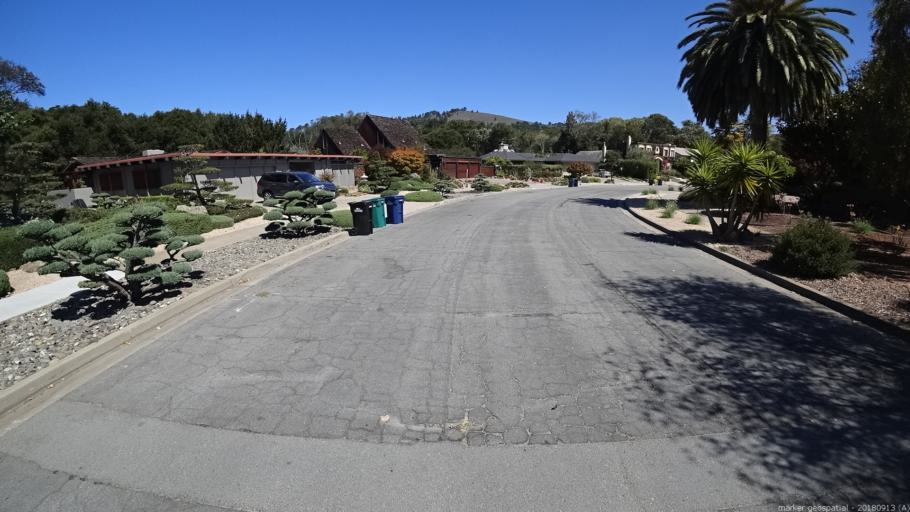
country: US
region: California
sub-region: Monterey County
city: Carmel-by-the-Sea
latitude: 36.5361
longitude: -121.8685
